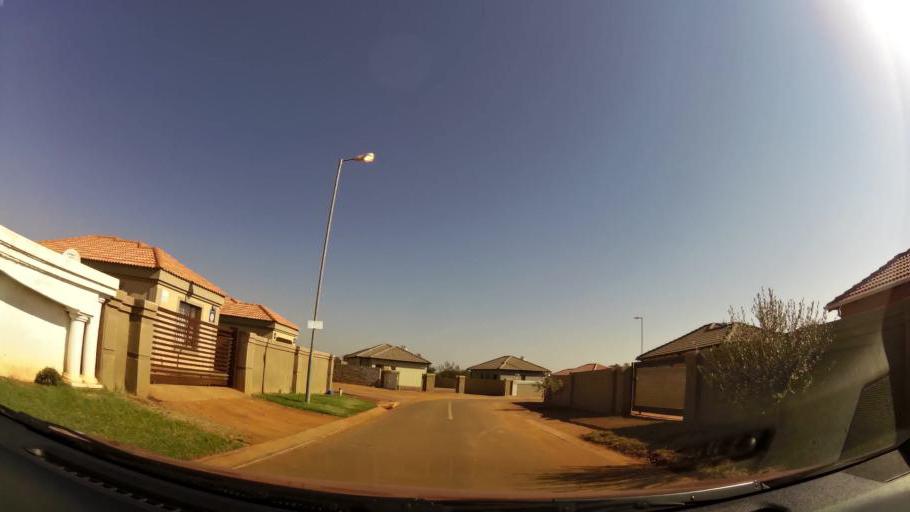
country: ZA
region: North-West
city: Ga-Rankuwa
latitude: -25.6338
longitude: 28.0738
